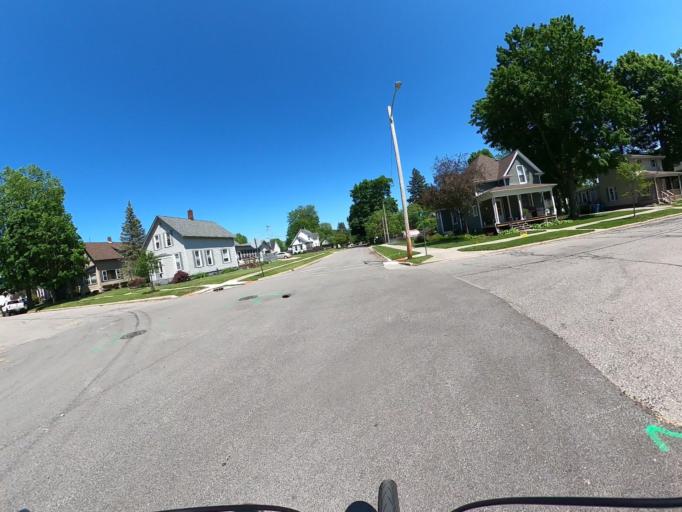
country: US
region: Indiana
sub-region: LaPorte County
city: LaPorte
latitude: 41.6047
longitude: -86.7278
